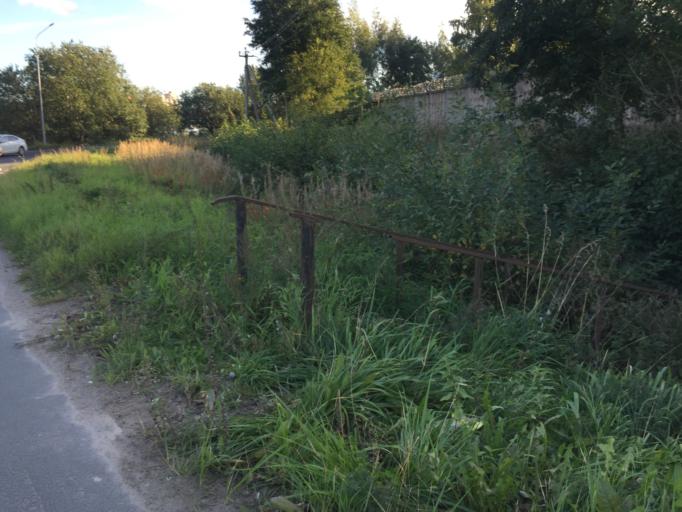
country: RU
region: Leningrad
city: Murino
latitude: 60.0570
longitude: 30.4597
